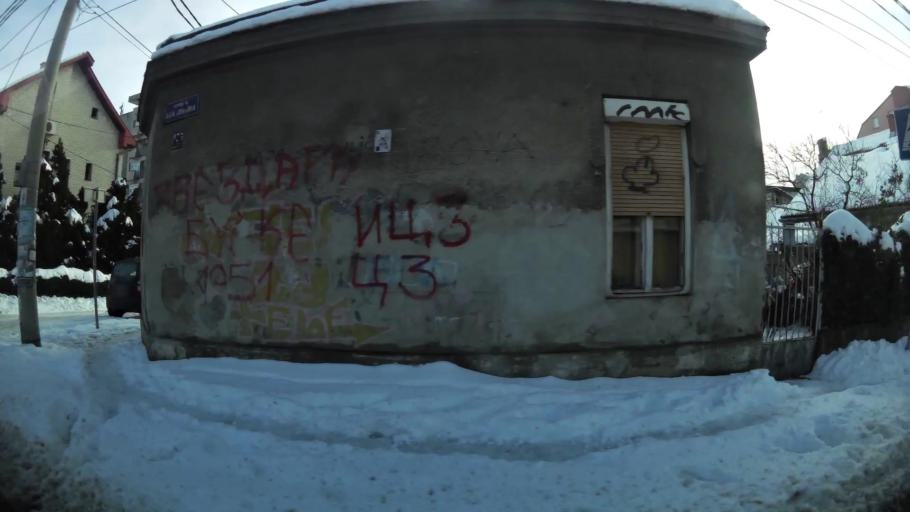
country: RS
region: Central Serbia
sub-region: Belgrade
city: Palilula
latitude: 44.8034
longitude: 20.4952
